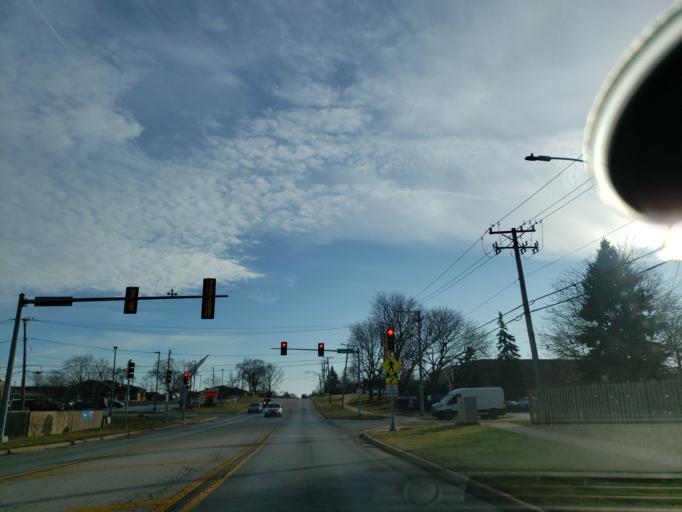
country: US
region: Illinois
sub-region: Cook County
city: Oak Forest
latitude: 41.6083
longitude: -87.7562
